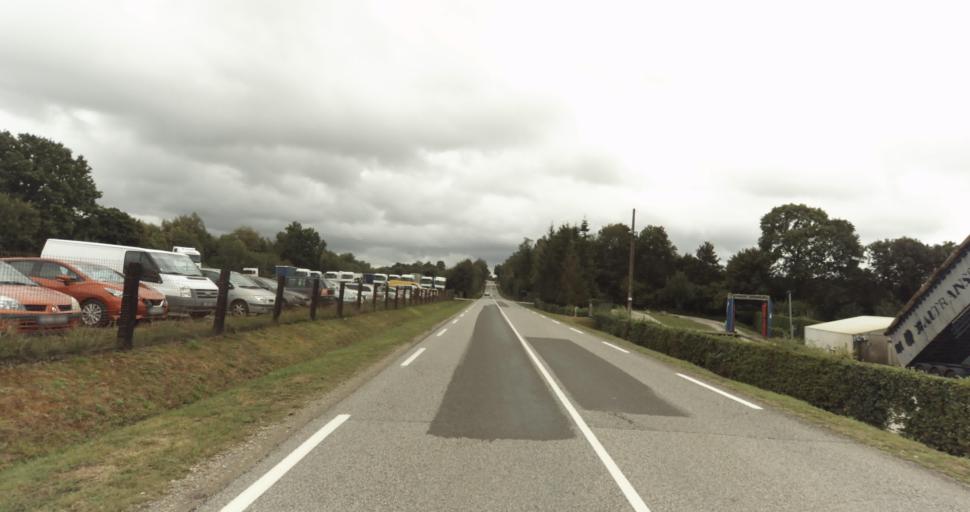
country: FR
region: Lower Normandy
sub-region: Departement de l'Orne
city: Sainte-Gauburge-Sainte-Colombe
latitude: 48.7040
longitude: 0.4377
